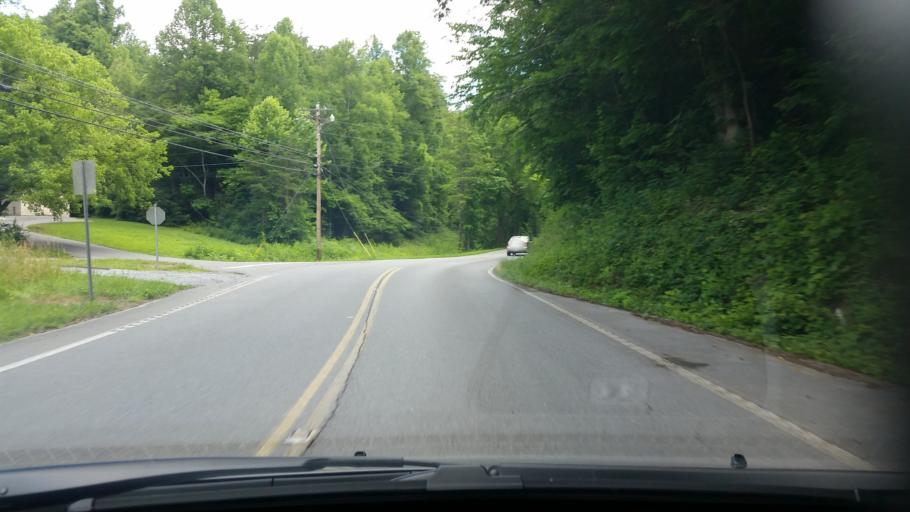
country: US
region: Tennessee
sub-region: Sevier County
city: Gatlinburg
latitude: 35.7366
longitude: -83.4672
